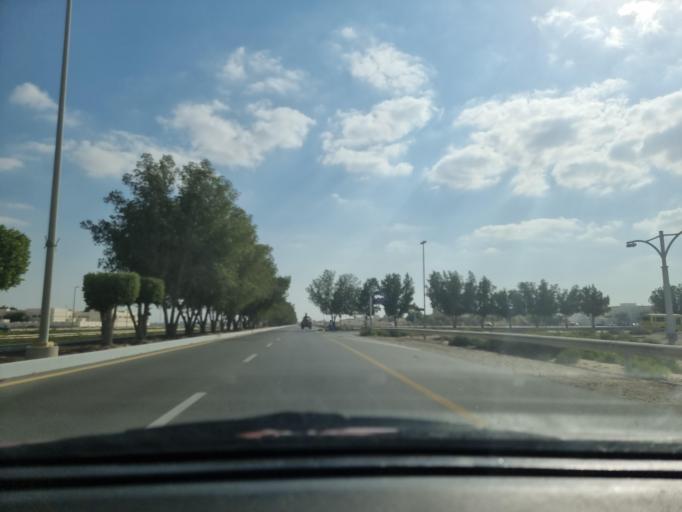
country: AE
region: Abu Dhabi
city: Abu Dhabi
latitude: 24.3874
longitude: 54.7049
